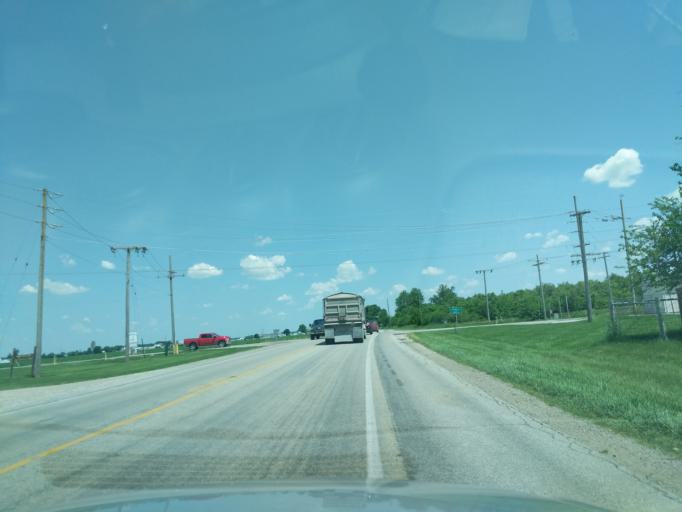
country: US
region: Indiana
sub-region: LaGrange County
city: Topeka
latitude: 41.5238
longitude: -85.5780
